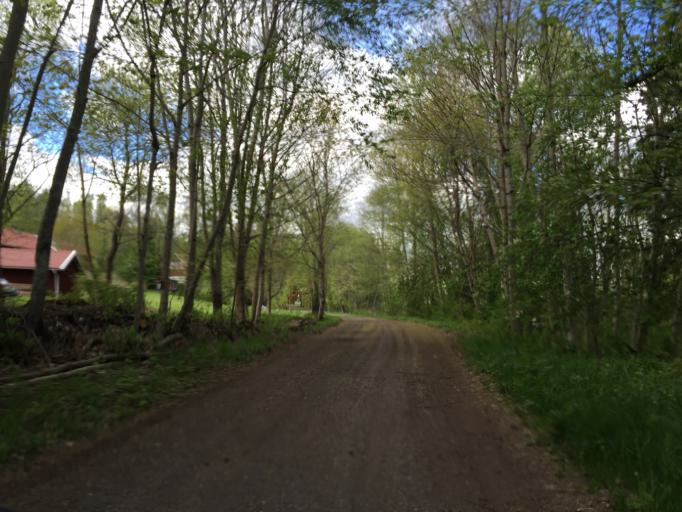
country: SE
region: Dalarna
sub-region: Ludvika Kommun
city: Ludvika
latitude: 60.2024
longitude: 15.2190
